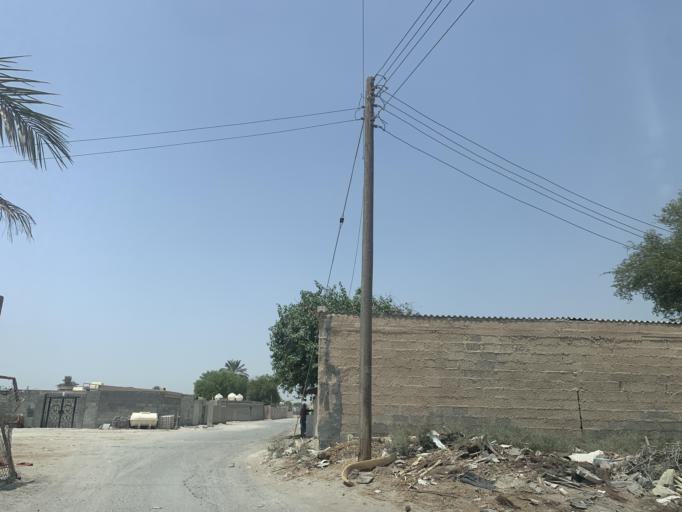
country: BH
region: Central Governorate
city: Madinat Hamad
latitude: 26.1550
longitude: 50.4964
